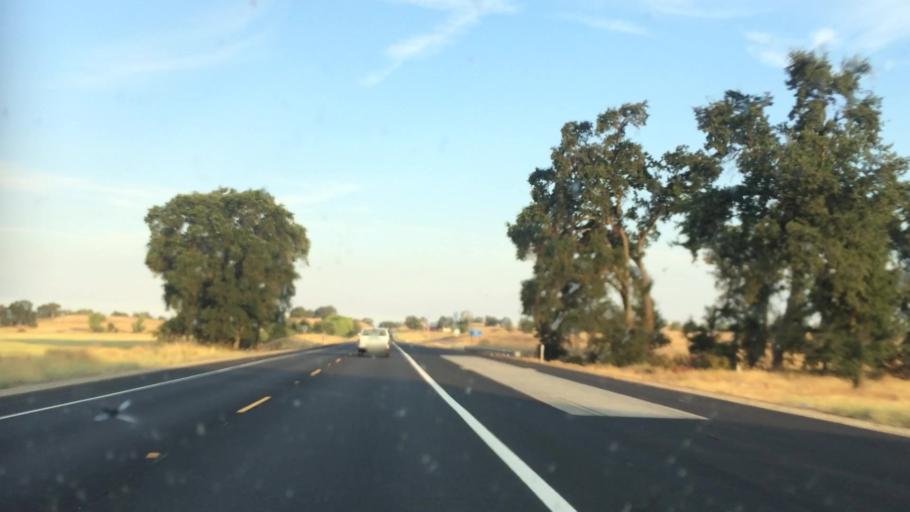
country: US
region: California
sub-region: Amador County
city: Plymouth
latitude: 38.4508
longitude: -120.9053
